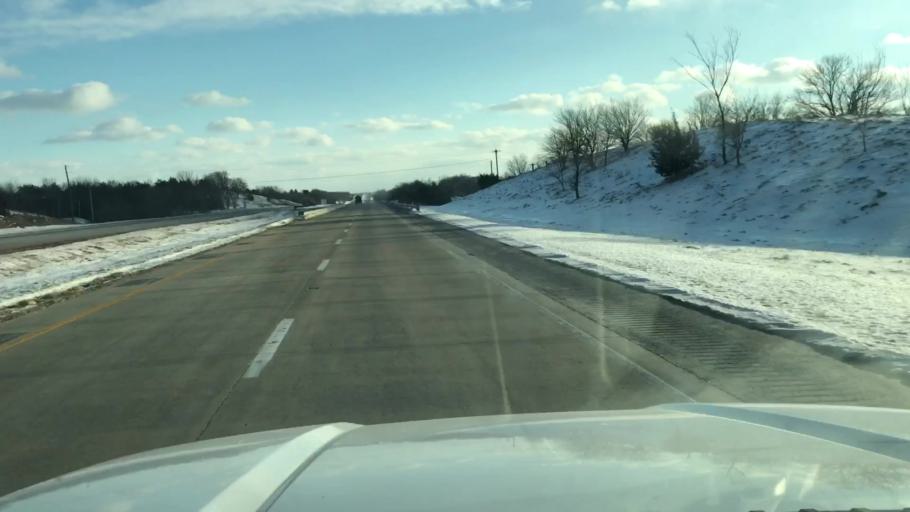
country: US
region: Missouri
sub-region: Andrew County
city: Savannah
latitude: 39.9502
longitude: -94.8603
